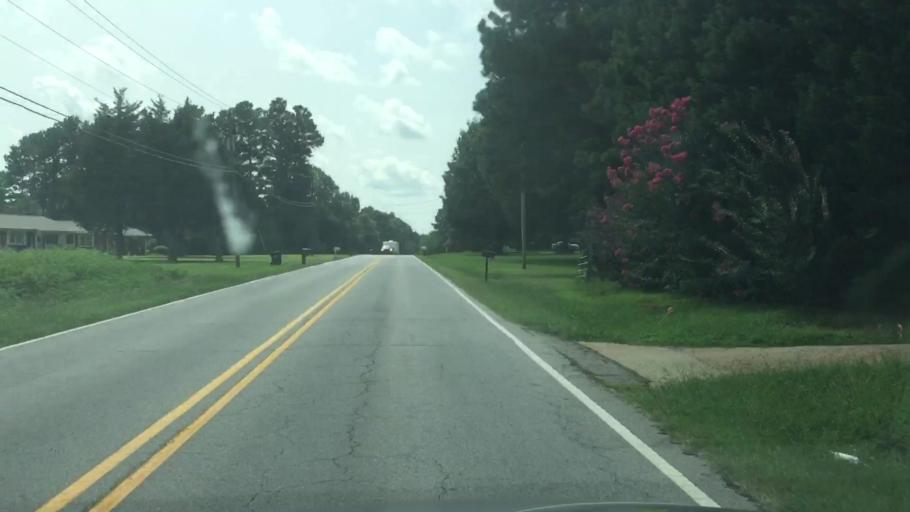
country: US
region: North Carolina
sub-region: Rowan County
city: China Grove
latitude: 35.6517
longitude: -80.5977
